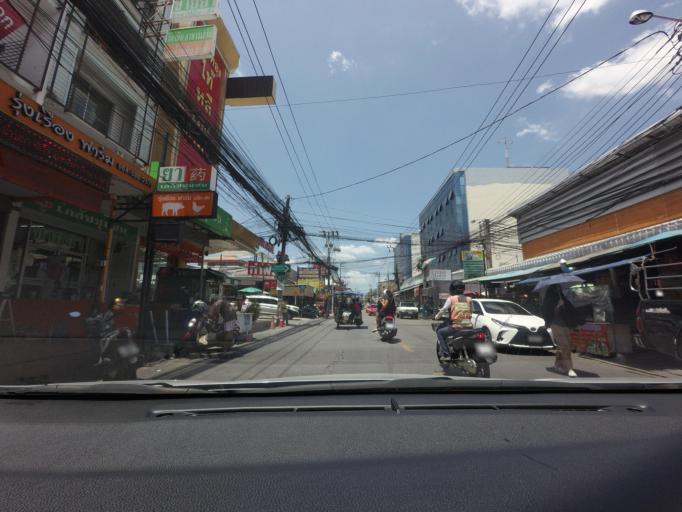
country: TH
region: Bangkok
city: Bang Na
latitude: 13.6924
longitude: 100.6395
